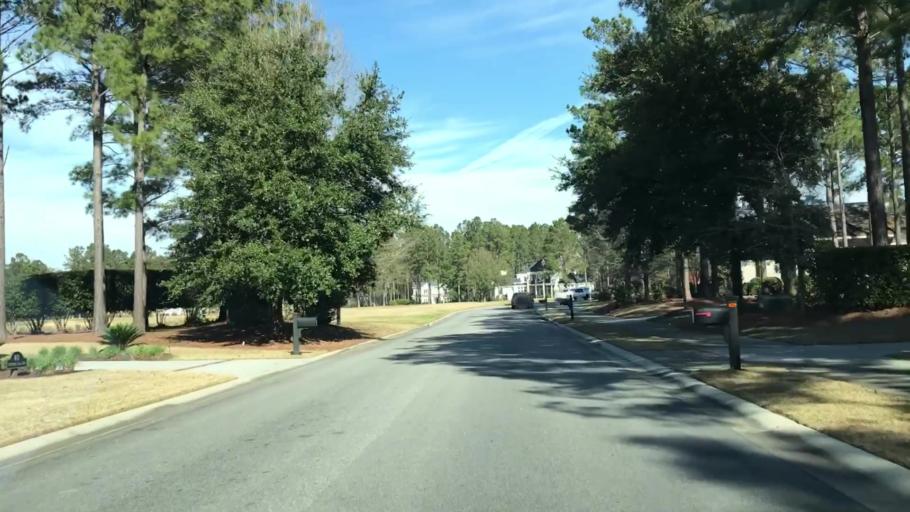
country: US
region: South Carolina
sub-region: Beaufort County
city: Bluffton
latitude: 32.2551
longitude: -80.9081
